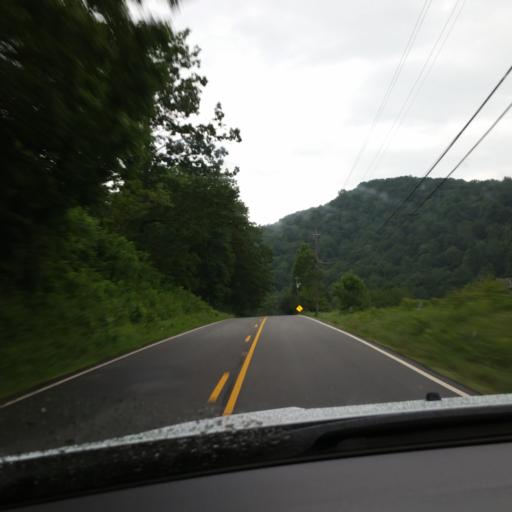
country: US
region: North Carolina
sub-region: Yancey County
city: Burnsville
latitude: 35.7744
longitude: -82.1992
